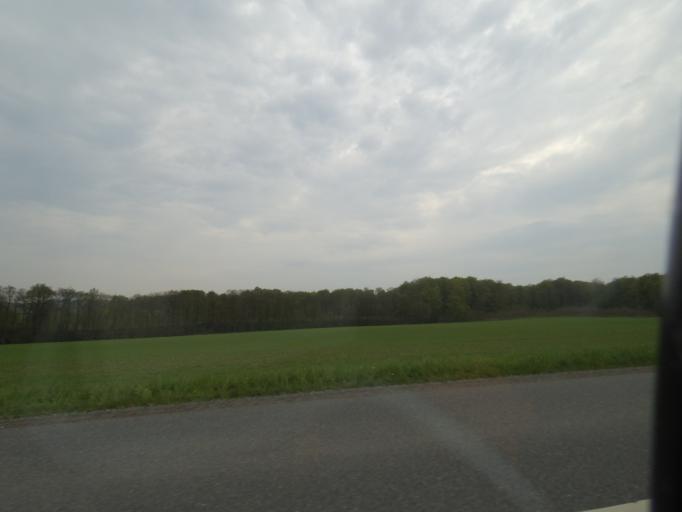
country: DK
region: South Denmark
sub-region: Svendborg Kommune
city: Svendborg
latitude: 55.1625
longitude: 10.6477
